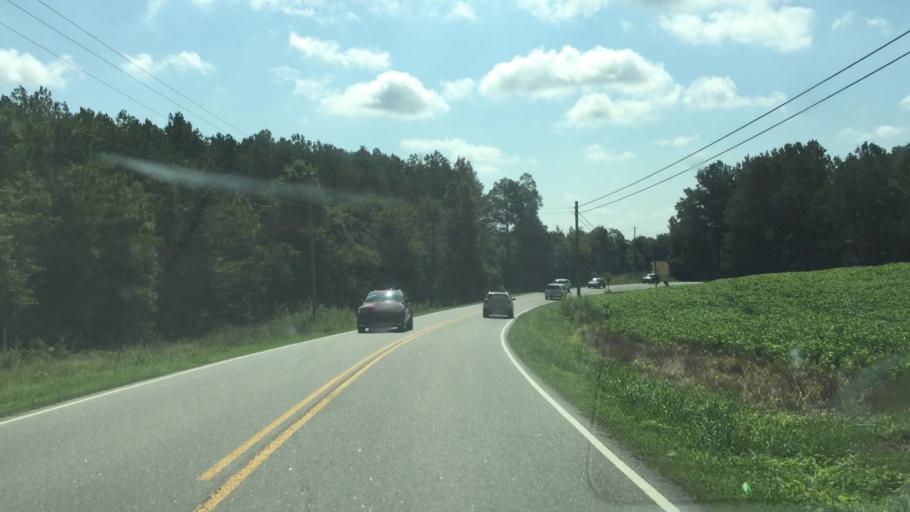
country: US
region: North Carolina
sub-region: Anson County
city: Polkton
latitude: 35.0304
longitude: -80.2371
